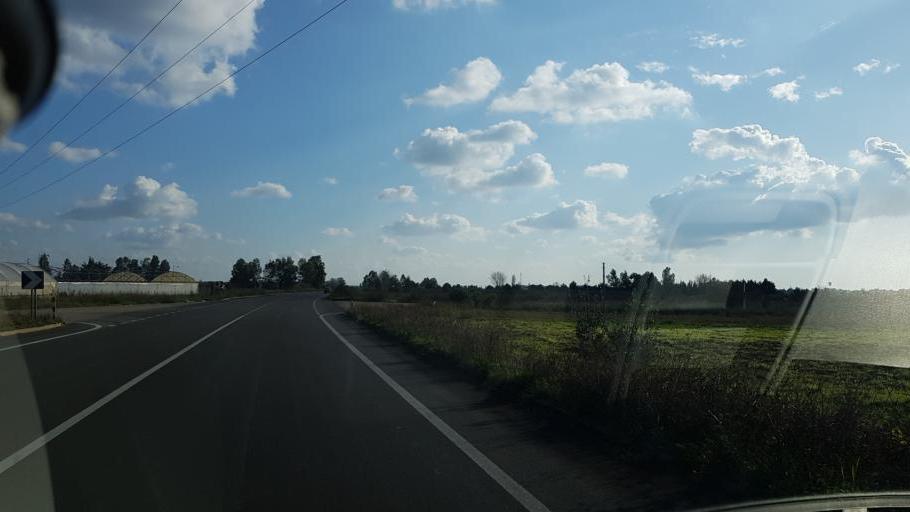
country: IT
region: Apulia
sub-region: Provincia di Lecce
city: Veglie
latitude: 40.3466
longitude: 17.9744
